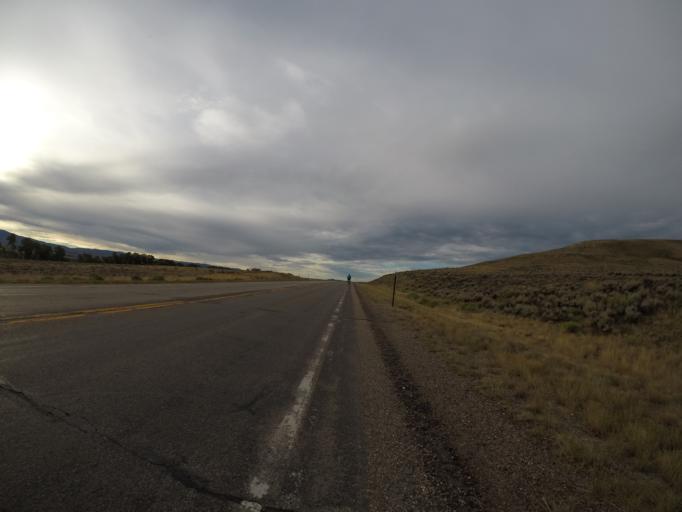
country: US
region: Wyoming
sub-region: Carbon County
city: Saratoga
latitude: 41.4070
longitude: -106.7769
